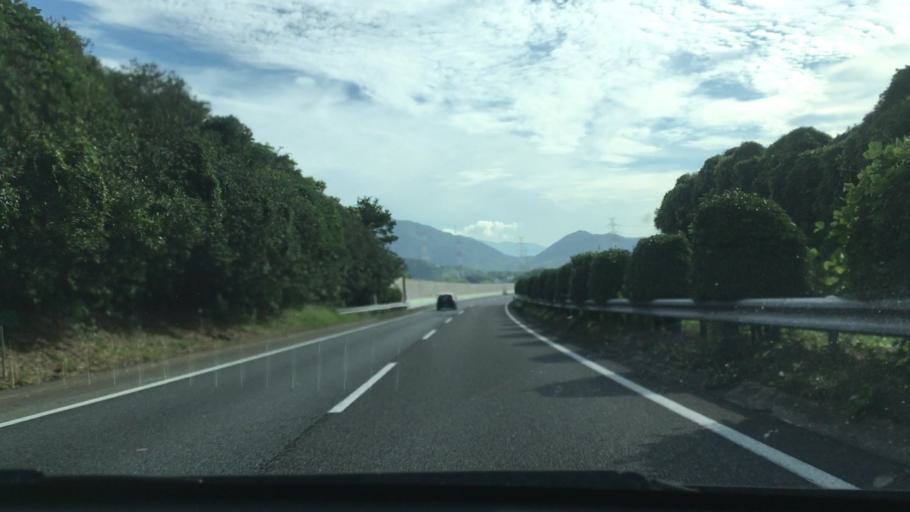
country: JP
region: Fukuoka
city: Kanda
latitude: 33.8374
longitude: 130.9242
